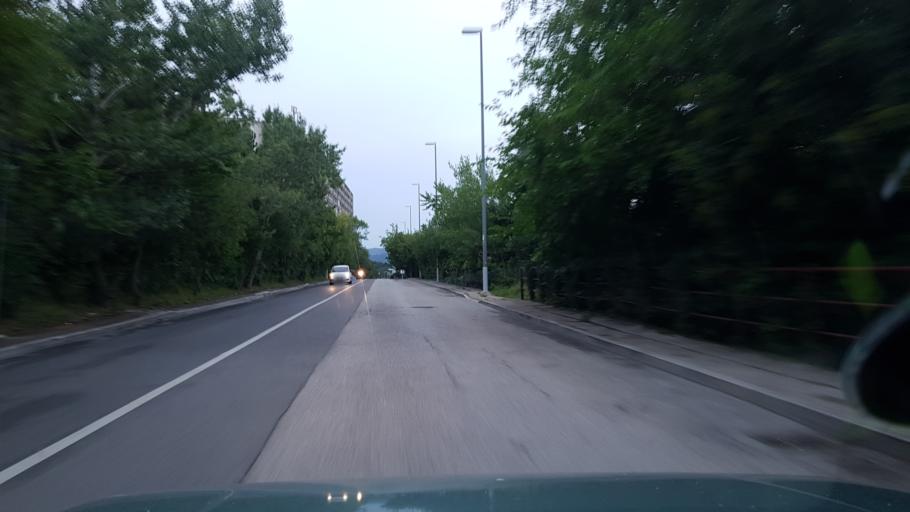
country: IT
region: Friuli Venezia Giulia
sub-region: Provincia di Trieste
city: Domio
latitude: 45.6384
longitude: 13.8287
